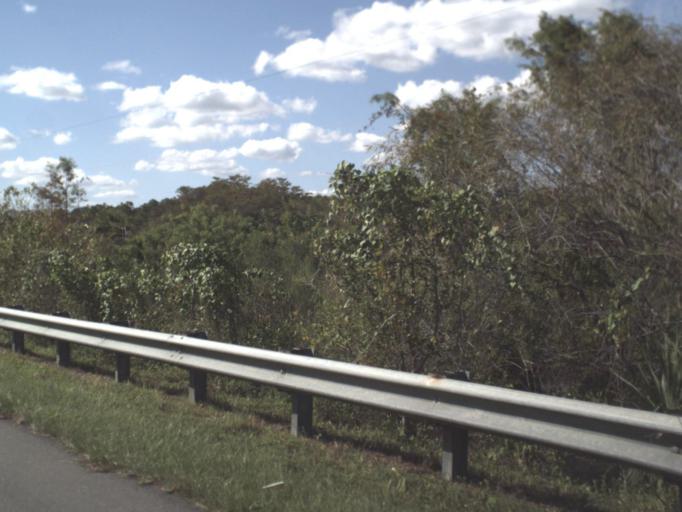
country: US
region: Florida
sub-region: Collier County
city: Lely Resort
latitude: 25.8657
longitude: -81.1202
